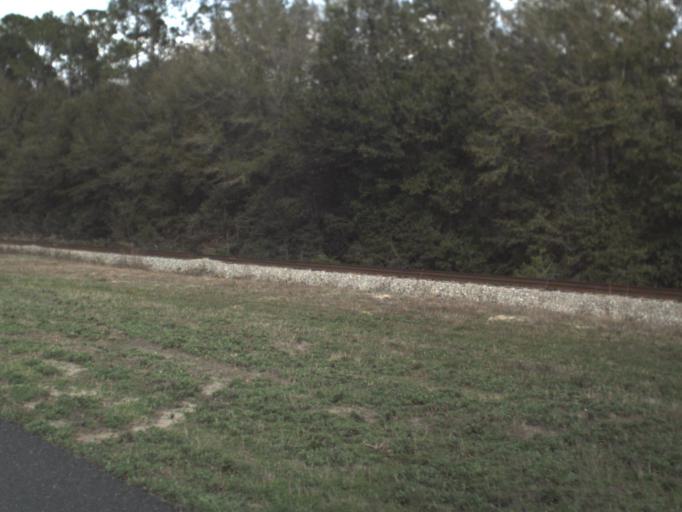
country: US
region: Florida
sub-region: Bay County
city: Youngstown
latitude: 30.4442
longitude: -85.4259
